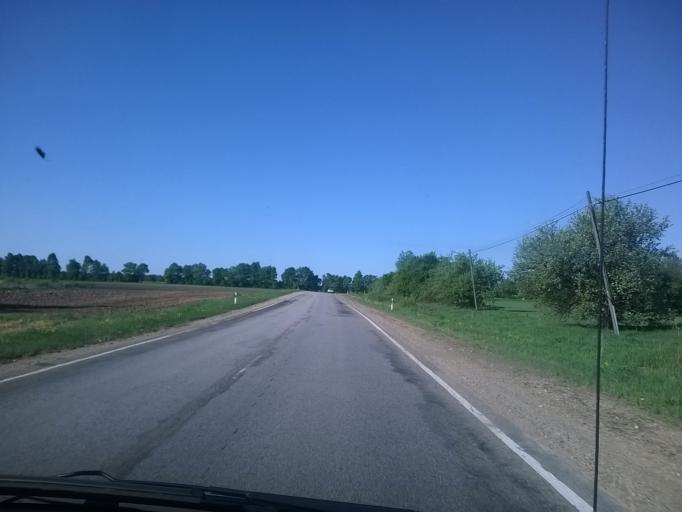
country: LV
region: Valkas Rajons
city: Valka
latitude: 57.7501
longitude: 25.9650
